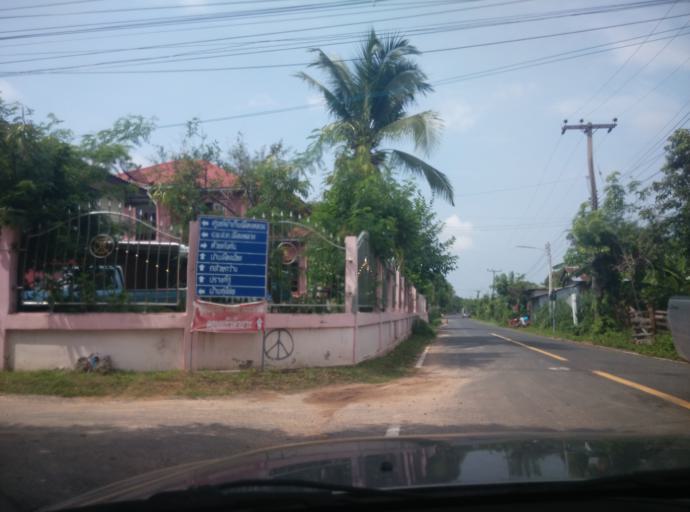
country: TH
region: Sisaket
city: Huai Thap Than
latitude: 15.0281
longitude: 104.0740
